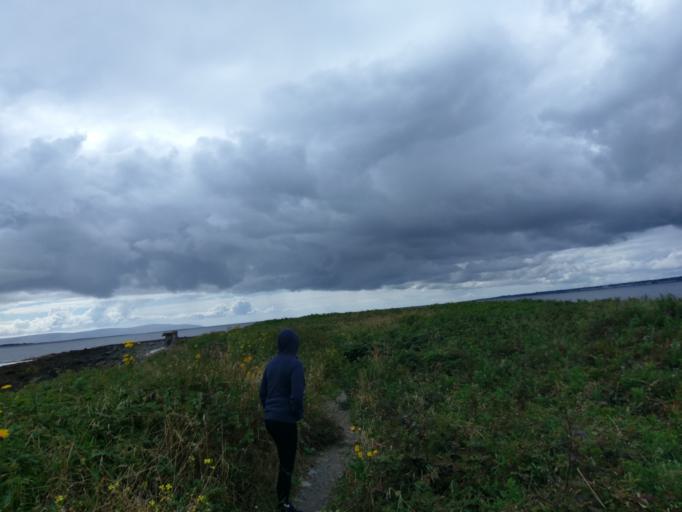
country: IE
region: Connaught
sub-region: County Galway
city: Gaillimh
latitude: 53.2472
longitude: -8.9883
